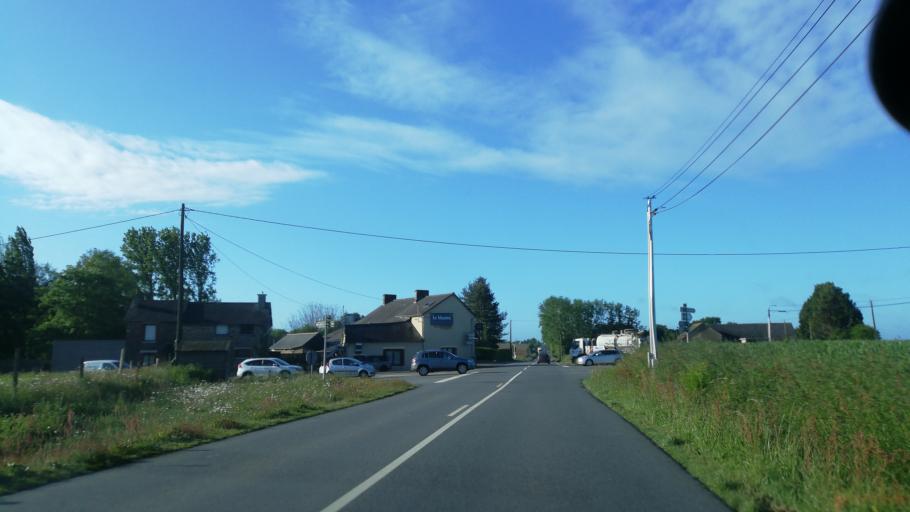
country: FR
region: Brittany
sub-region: Departement d'Ille-et-Vilaine
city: Bedee
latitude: 48.2089
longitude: -1.9416
